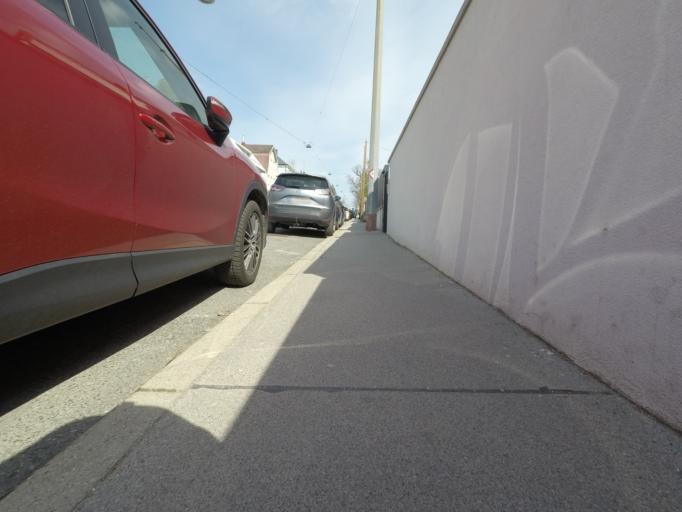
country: AT
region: Lower Austria
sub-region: Politischer Bezirk Modling
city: Perchtoldsdorf
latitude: 48.1669
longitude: 16.2576
